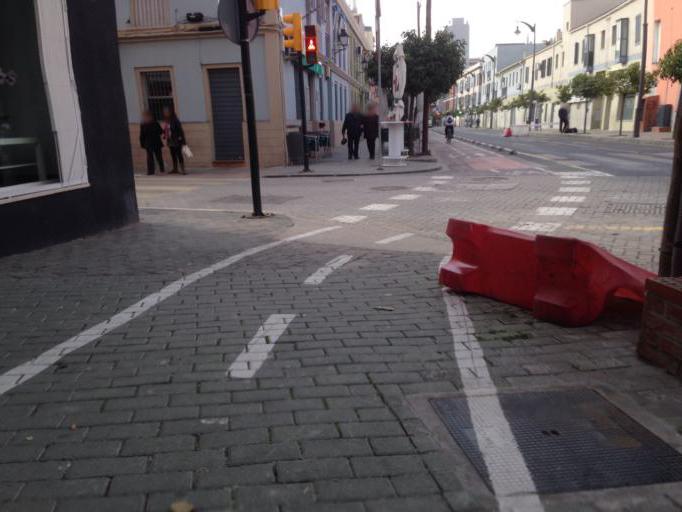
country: ES
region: Andalusia
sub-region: Provincia de Malaga
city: Malaga
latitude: 36.7236
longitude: -4.4288
